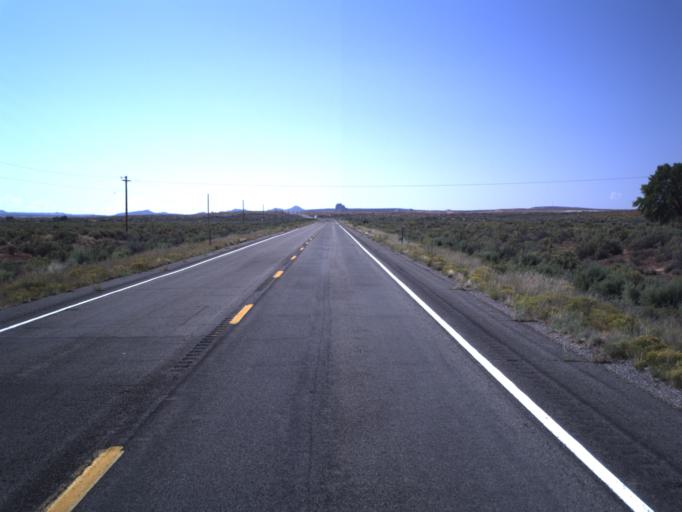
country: US
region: Utah
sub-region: San Juan County
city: Blanding
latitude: 37.1051
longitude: -109.5467
